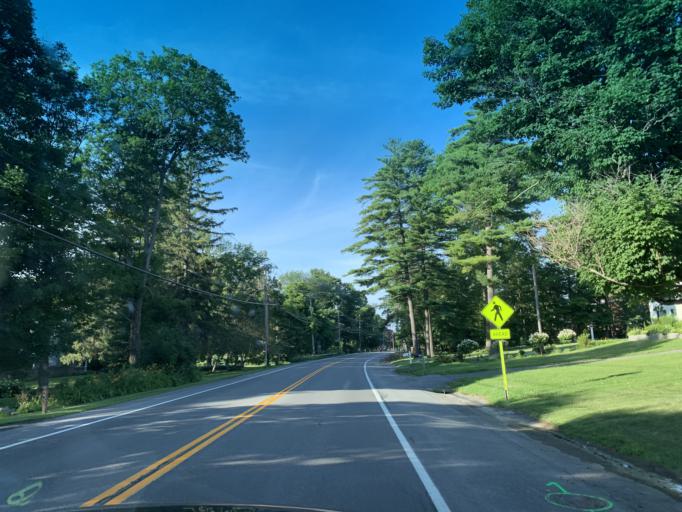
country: US
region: New York
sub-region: Oneida County
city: Clinton
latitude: 43.0555
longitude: -75.3664
